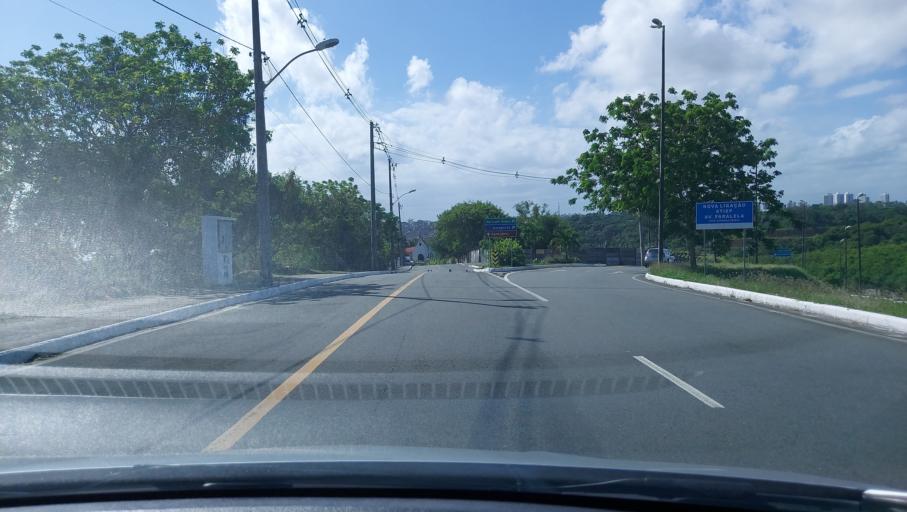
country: BR
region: Bahia
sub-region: Salvador
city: Salvador
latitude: -12.9771
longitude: -38.4459
